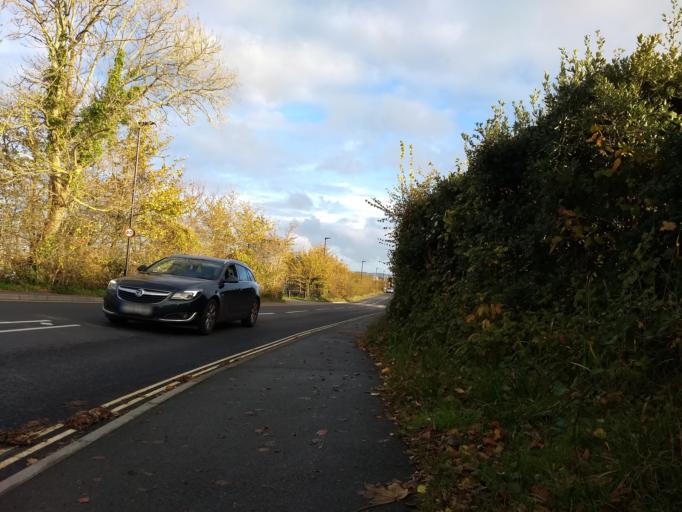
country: GB
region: England
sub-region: Isle of Wight
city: Yarmouth
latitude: 50.7052
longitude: -1.5097
